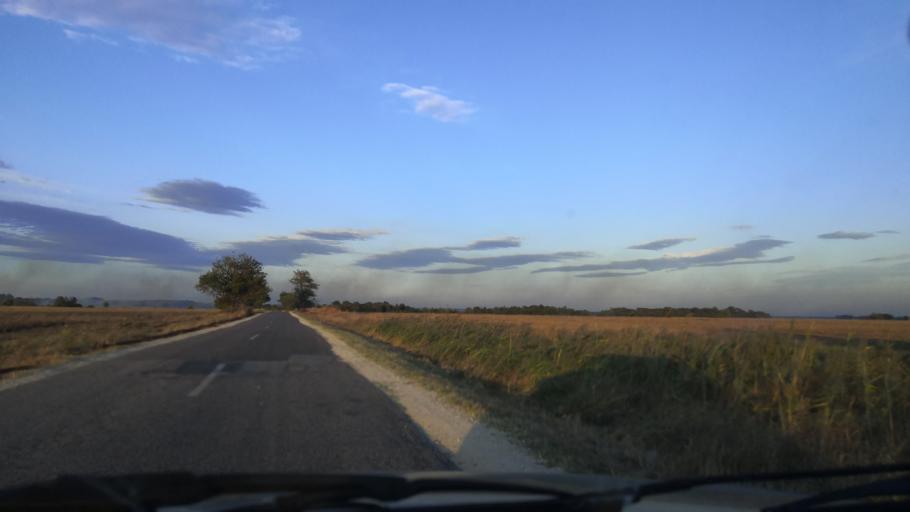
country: RS
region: Central Serbia
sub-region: Borski Okrug
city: Negotin
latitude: 44.2463
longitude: 22.5780
